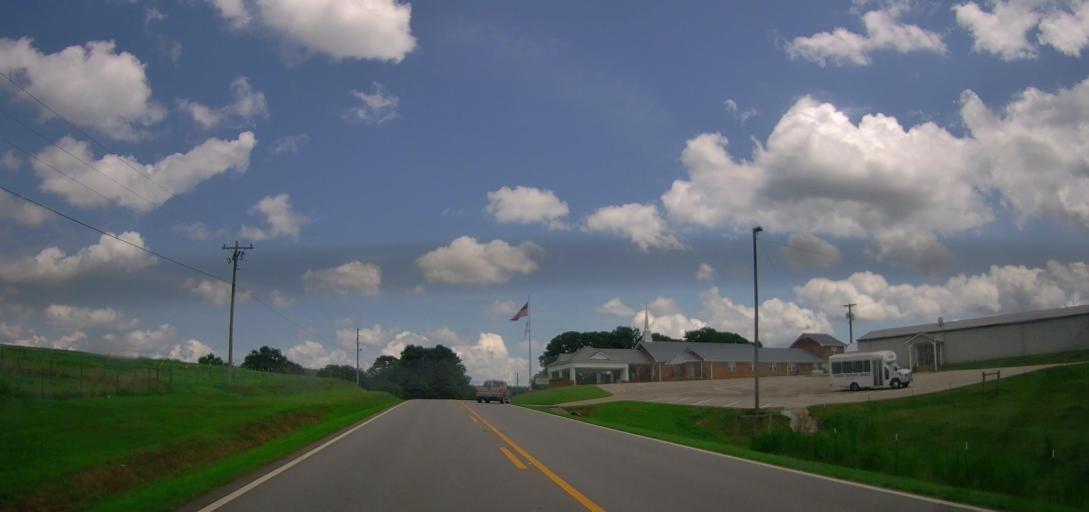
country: US
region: Georgia
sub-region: Carroll County
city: Bowdon
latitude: 33.4441
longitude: -85.2833
